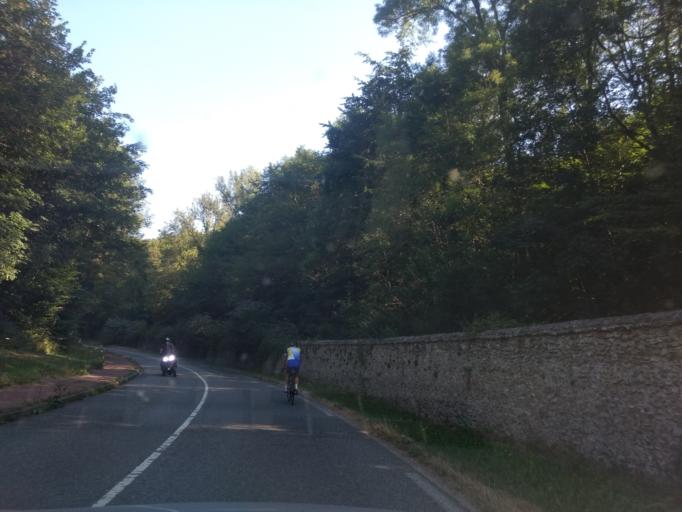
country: FR
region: Ile-de-France
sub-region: Departement des Yvelines
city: Jouy-en-Josas
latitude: 48.7736
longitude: 2.1731
